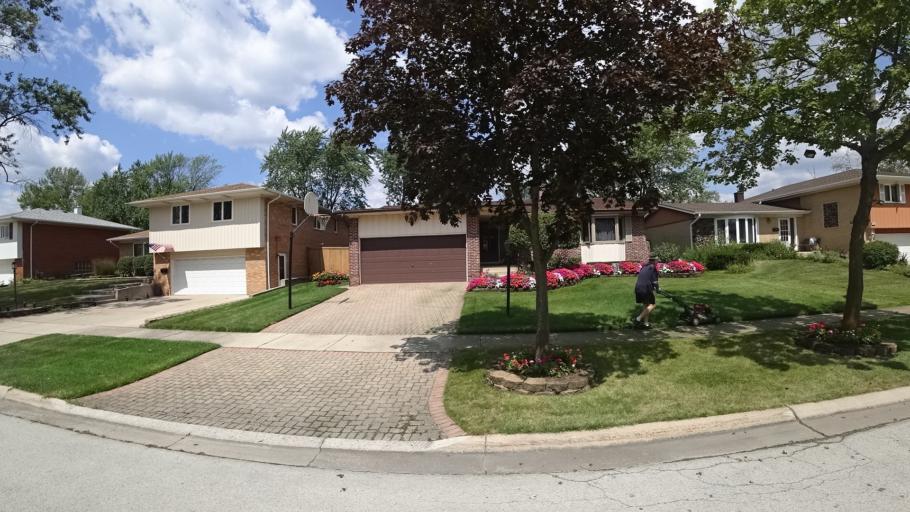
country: US
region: Illinois
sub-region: Cook County
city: Oak Forest
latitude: 41.6163
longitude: -87.7793
